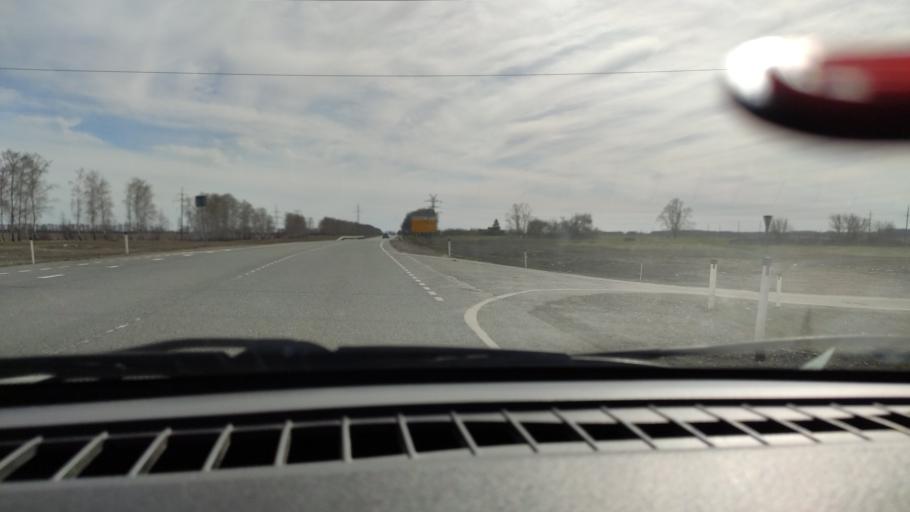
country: RU
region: Bashkortostan
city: Salavat
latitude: 53.4947
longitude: 55.8697
